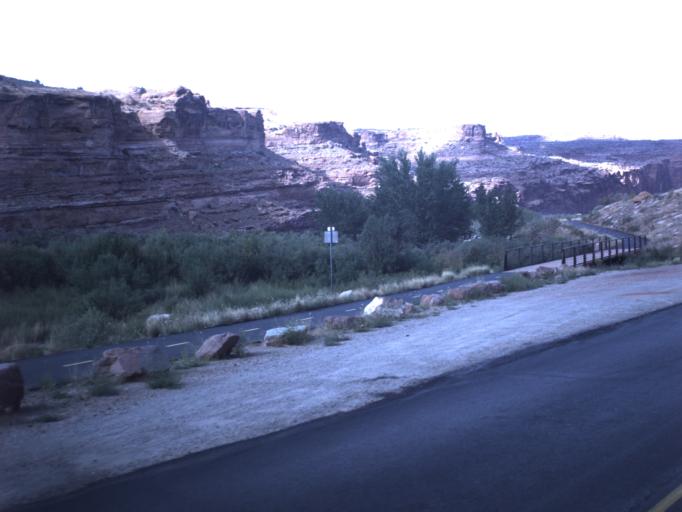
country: US
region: Utah
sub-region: Grand County
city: Moab
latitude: 38.6097
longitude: -109.5349
